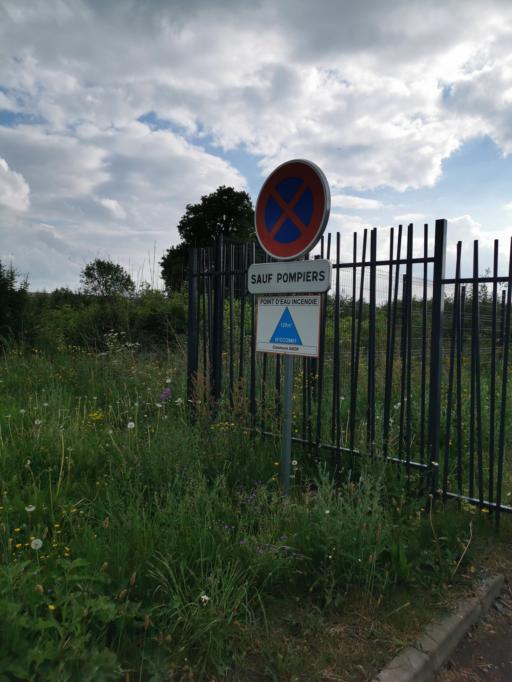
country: FR
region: Nord-Pas-de-Calais
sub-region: Departement du Nord
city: Anor
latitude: 49.9861
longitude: 4.0917
